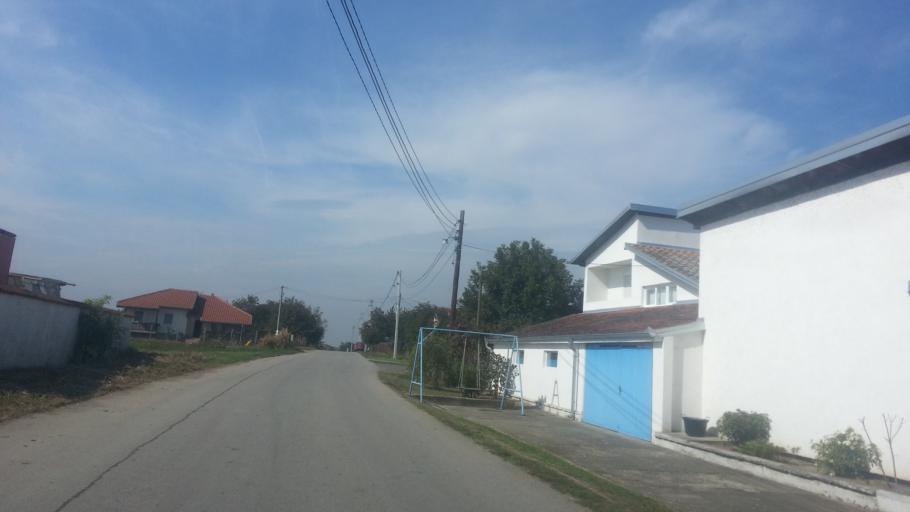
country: RS
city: Stari Banovci
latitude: 44.9928
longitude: 20.2904
